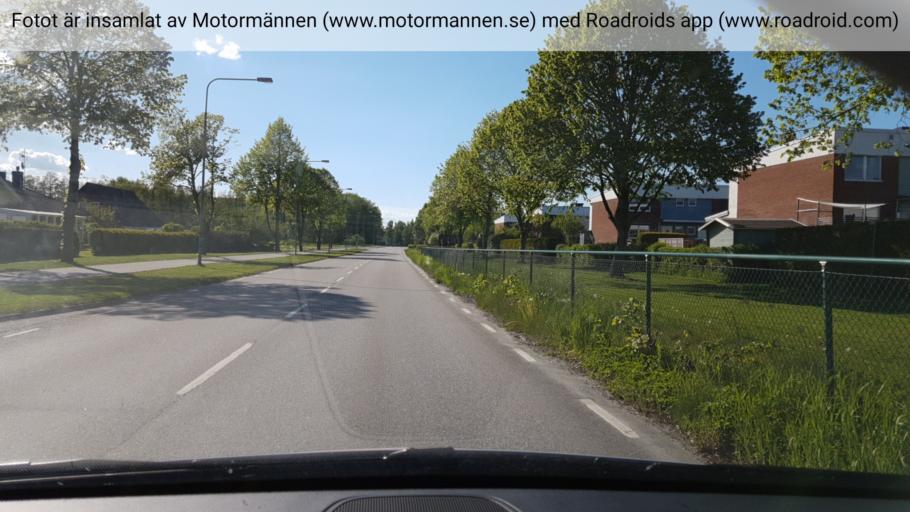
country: SE
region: Vaestra Goetaland
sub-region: Gotene Kommun
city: Kallby
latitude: 58.5090
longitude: 13.3050
